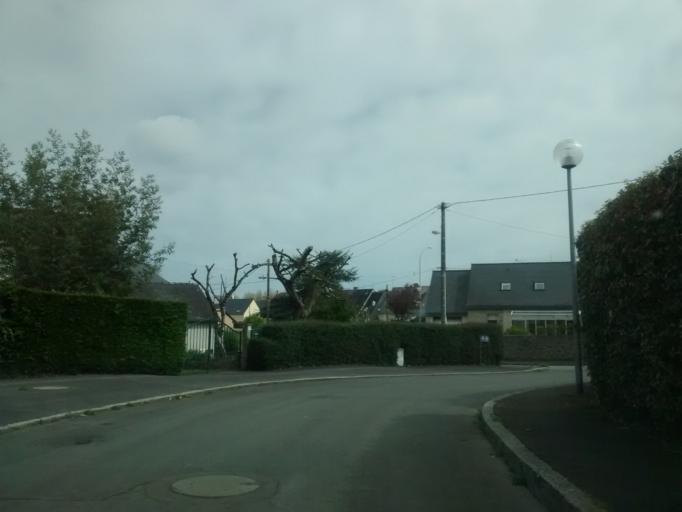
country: FR
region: Brittany
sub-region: Departement d'Ille-et-Vilaine
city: Dinard
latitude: 48.6297
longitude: -2.0766
